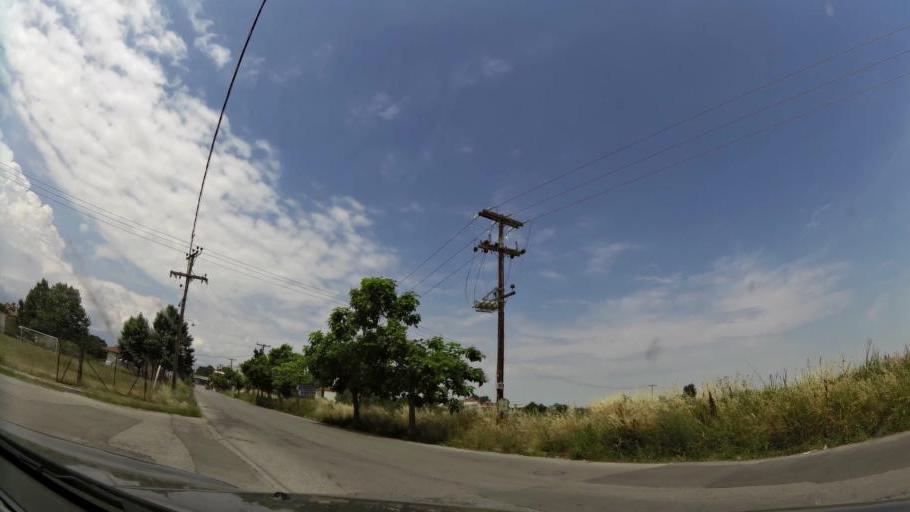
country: GR
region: Central Macedonia
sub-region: Nomos Pierias
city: Peristasi
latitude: 40.2643
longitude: 22.5356
